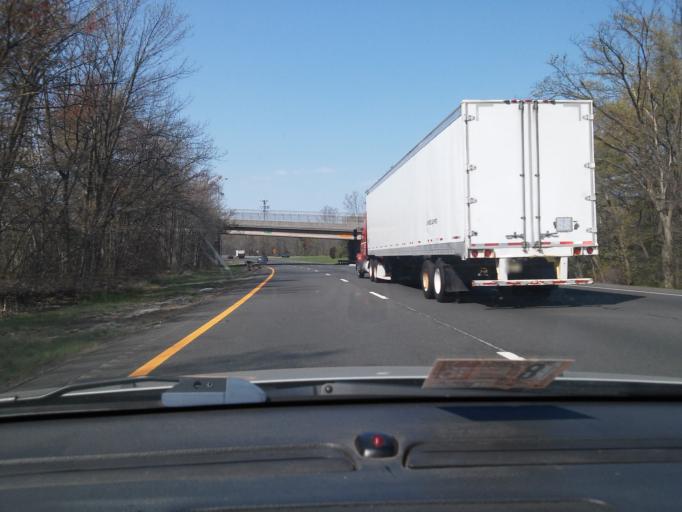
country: US
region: New Jersey
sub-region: Union County
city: Berkeley Heights
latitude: 40.6617
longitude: -74.4336
